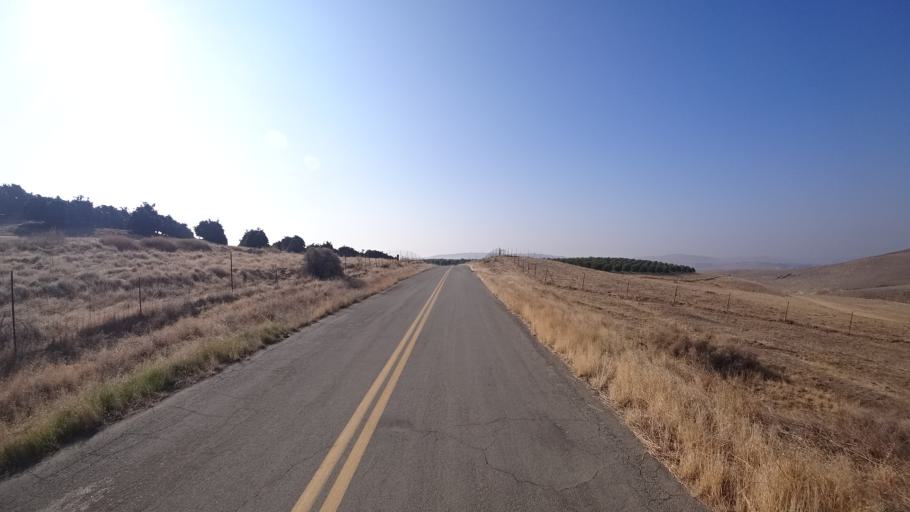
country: US
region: California
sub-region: Kern County
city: Oildale
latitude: 35.4374
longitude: -118.8276
